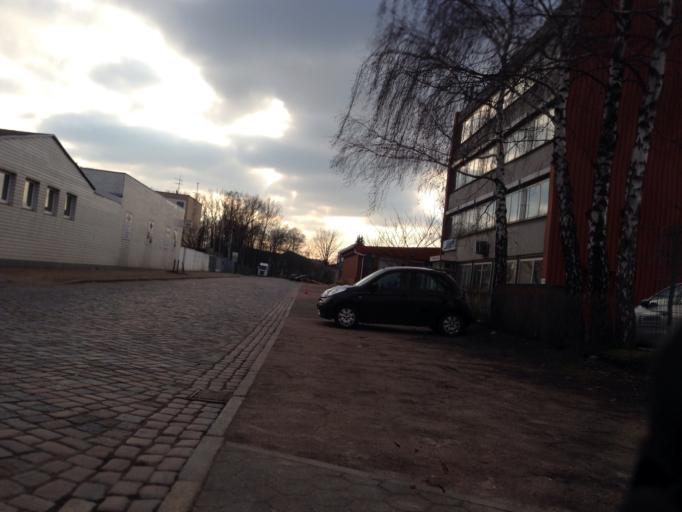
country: DE
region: Hamburg
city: Wandsbek
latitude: 53.5857
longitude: 10.0940
